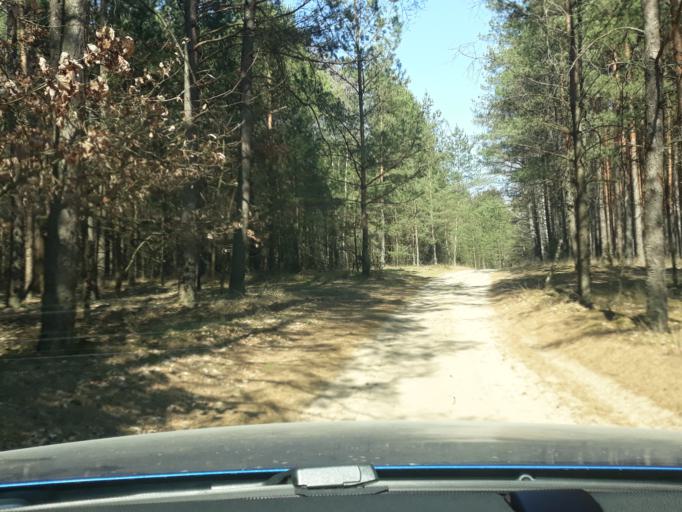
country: PL
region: Pomeranian Voivodeship
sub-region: Powiat bytowski
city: Lipnica
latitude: 53.8545
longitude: 17.4331
